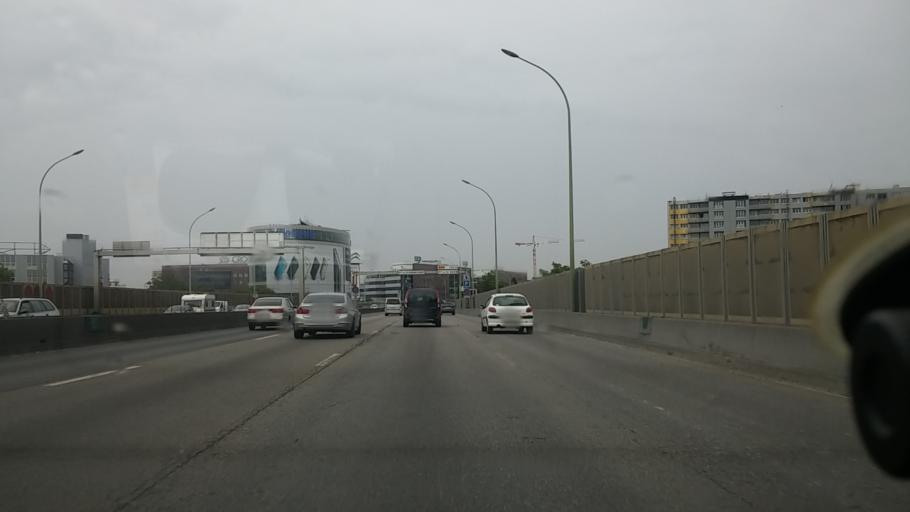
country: FR
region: Ile-de-France
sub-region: Departement des Hauts-de-Seine
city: Clichy
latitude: 48.8994
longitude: 2.3189
